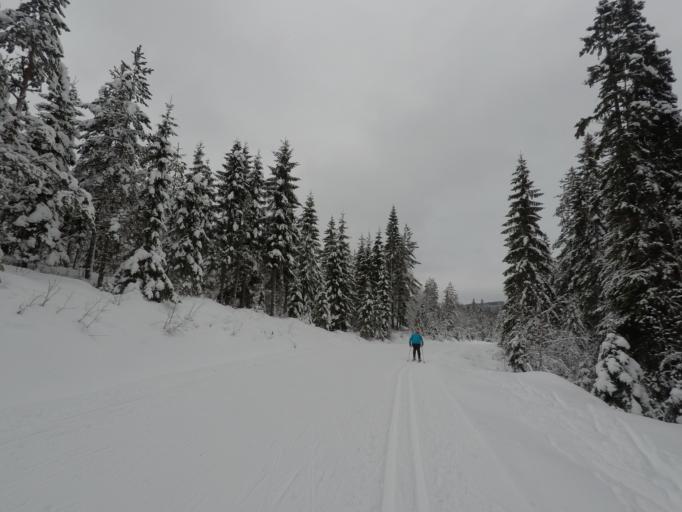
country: SE
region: Dalarna
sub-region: Ludvika Kommun
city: Abborrberget
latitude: 60.1462
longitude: 14.4833
